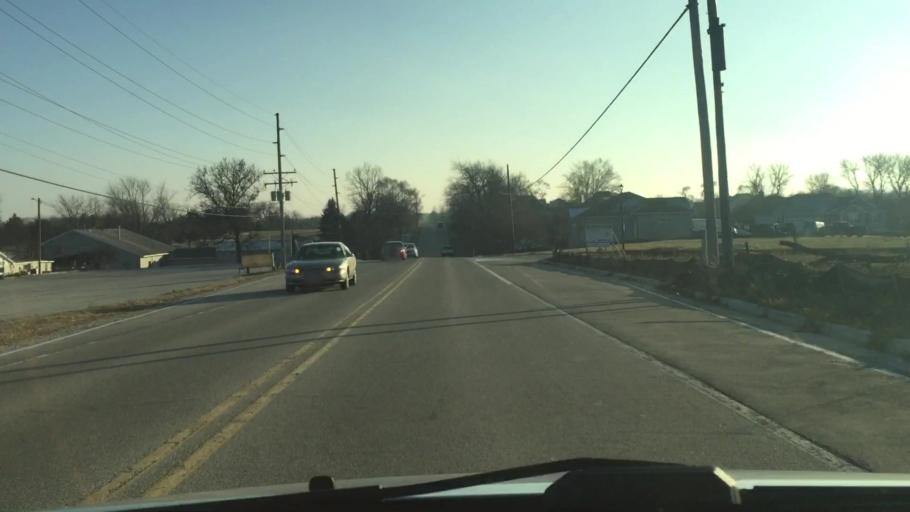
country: US
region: Wisconsin
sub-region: Waukesha County
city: Oconomowoc
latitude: 43.0895
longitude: -88.4957
